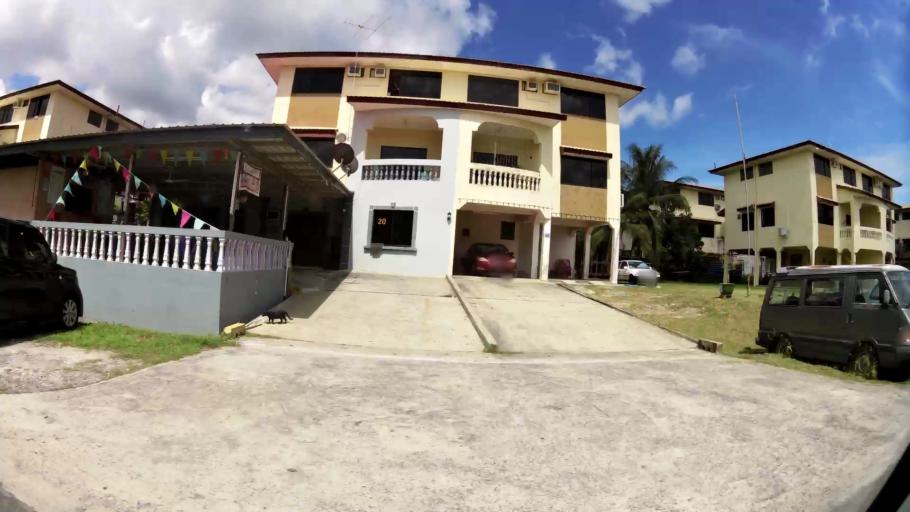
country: BN
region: Brunei and Muara
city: Bandar Seri Begawan
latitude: 4.9318
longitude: 114.8941
